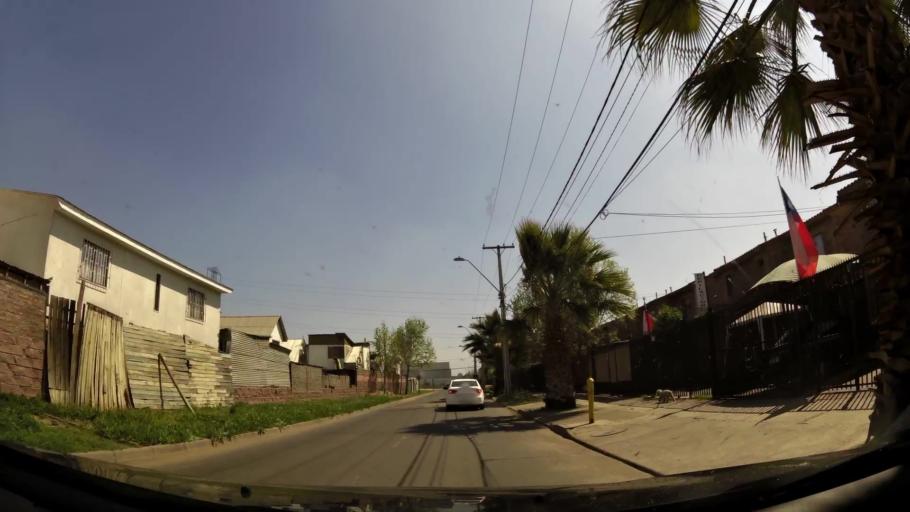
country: CL
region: Santiago Metropolitan
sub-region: Provincia de Santiago
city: Lo Prado
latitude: -33.3657
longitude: -70.7182
